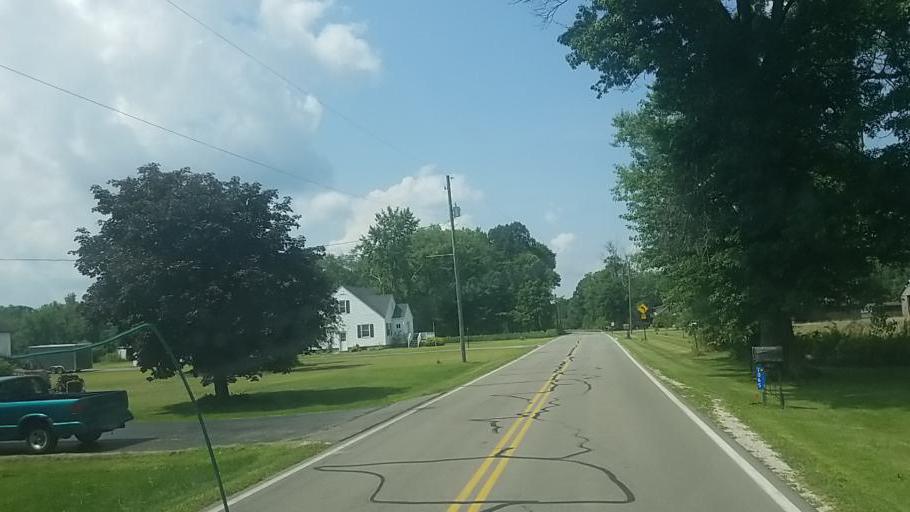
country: US
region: Ohio
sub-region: Crawford County
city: Crestline
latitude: 40.7980
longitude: -82.7792
